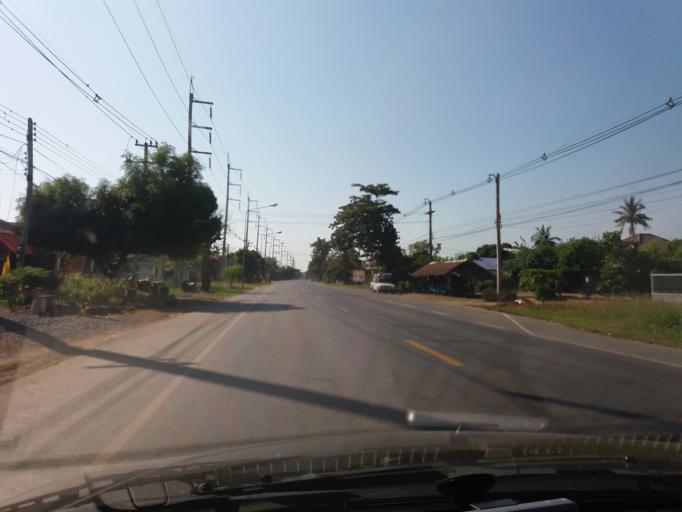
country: TH
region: Kamphaeng Phet
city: Khlong Khlung
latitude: 16.2883
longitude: 99.6986
